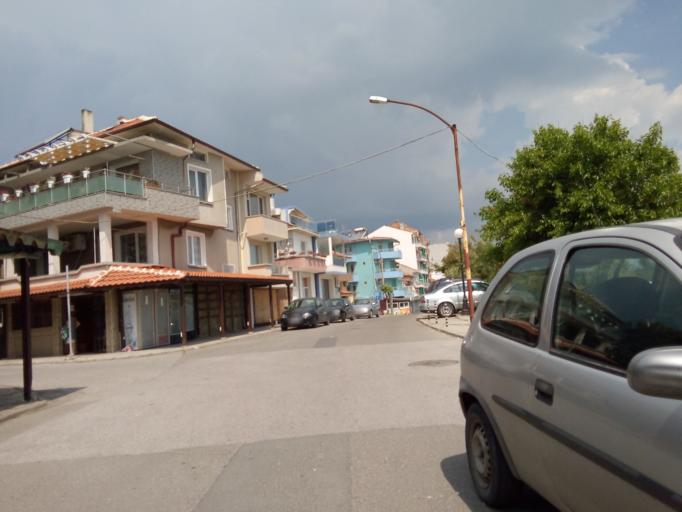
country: BG
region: Burgas
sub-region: Obshtina Pomorie
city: Pomorie
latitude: 42.5577
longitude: 27.6468
